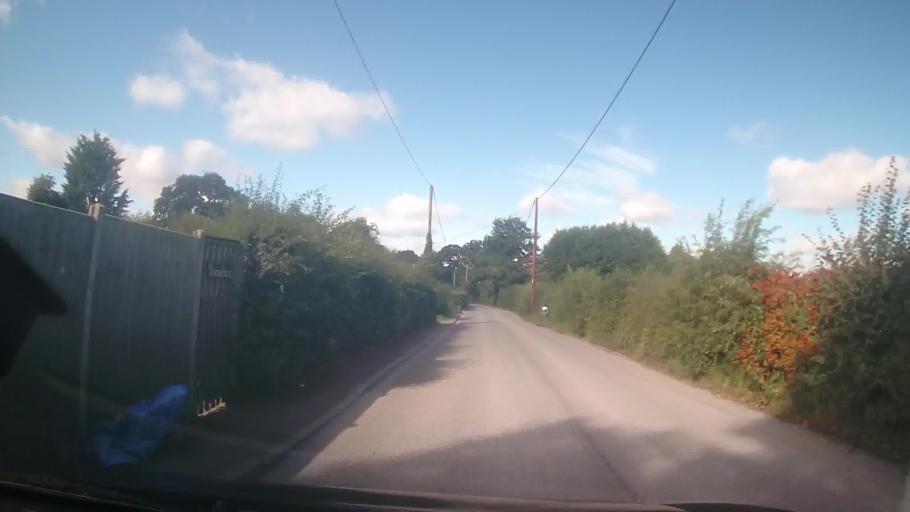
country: GB
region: England
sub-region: Shropshire
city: Bicton
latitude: 52.7626
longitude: -2.7962
